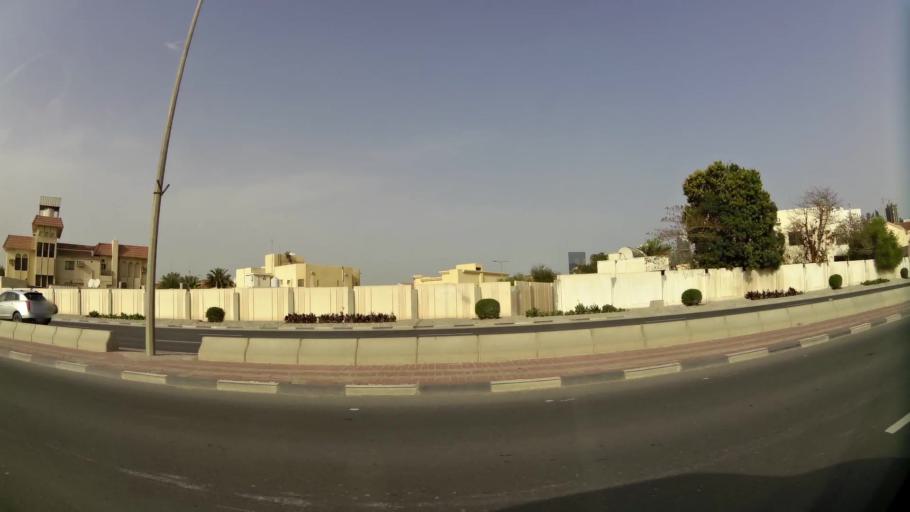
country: QA
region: Baladiyat ad Dawhah
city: Doha
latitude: 25.3252
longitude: 51.5087
